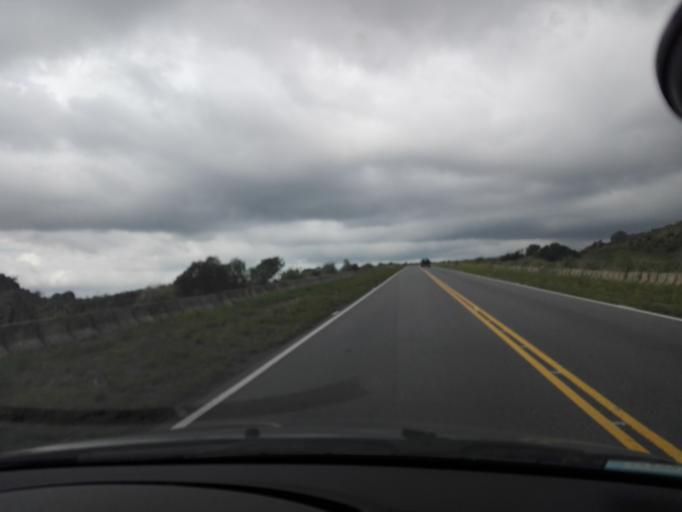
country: AR
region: Cordoba
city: Cuesta Blanca
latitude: -31.6021
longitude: -64.6753
